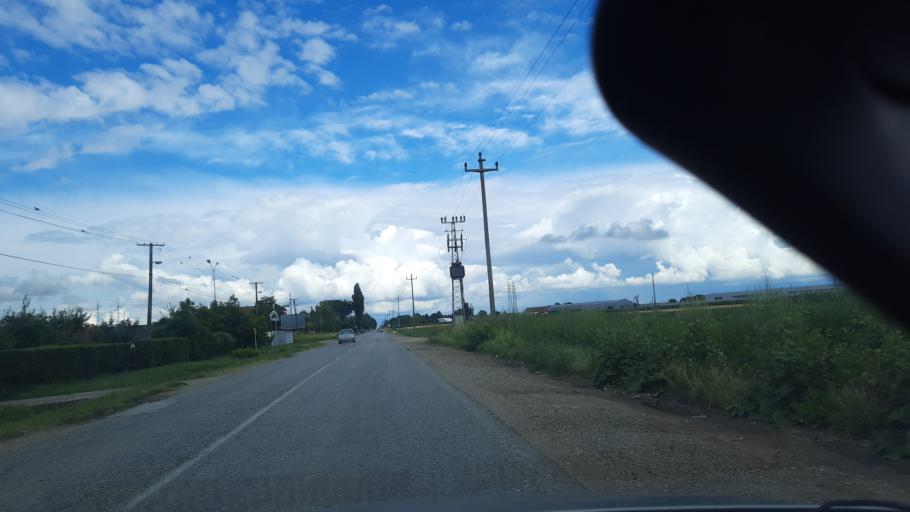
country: RS
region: Autonomna Pokrajina Vojvodina
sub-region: Sremski Okrug
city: Sremska Mitrovica
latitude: 44.9720
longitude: 19.6471
